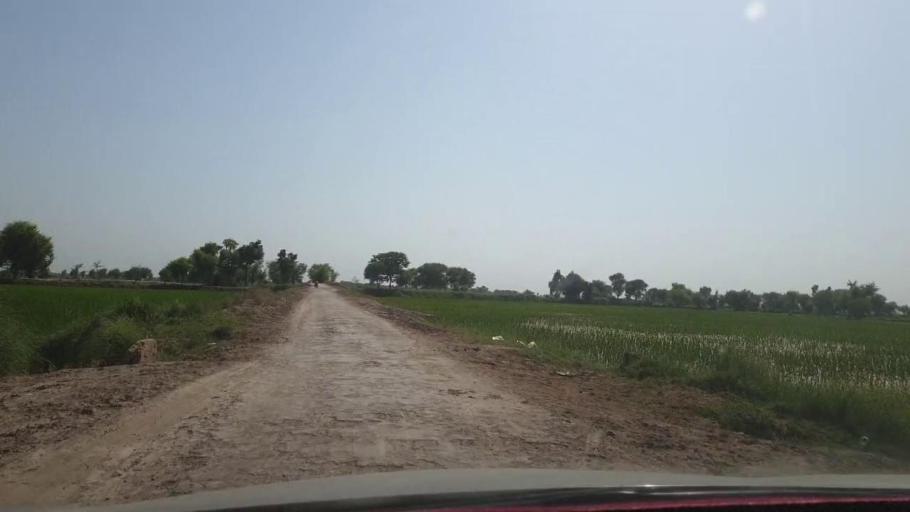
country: PK
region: Sindh
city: Nasirabad
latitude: 27.3540
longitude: 67.8443
